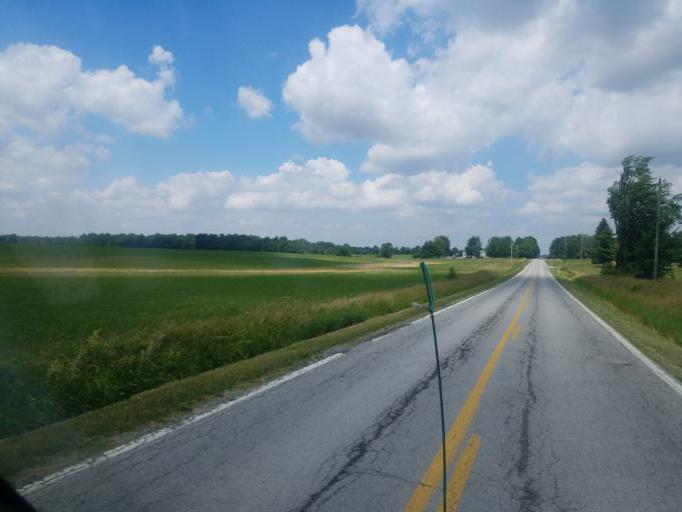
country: US
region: Ohio
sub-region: Huron County
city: Willard
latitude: 41.0754
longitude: -82.6840
